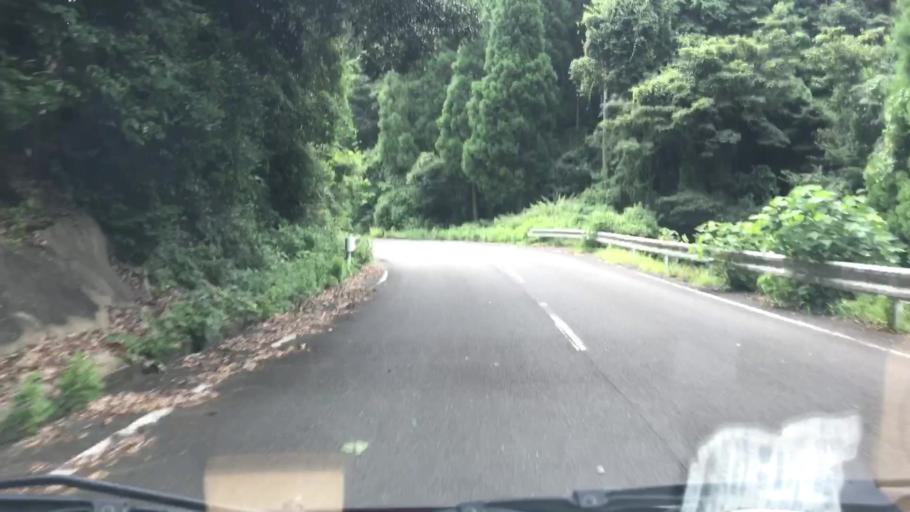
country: JP
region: Saga Prefecture
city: Takeocho-takeo
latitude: 33.2262
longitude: 130.0052
